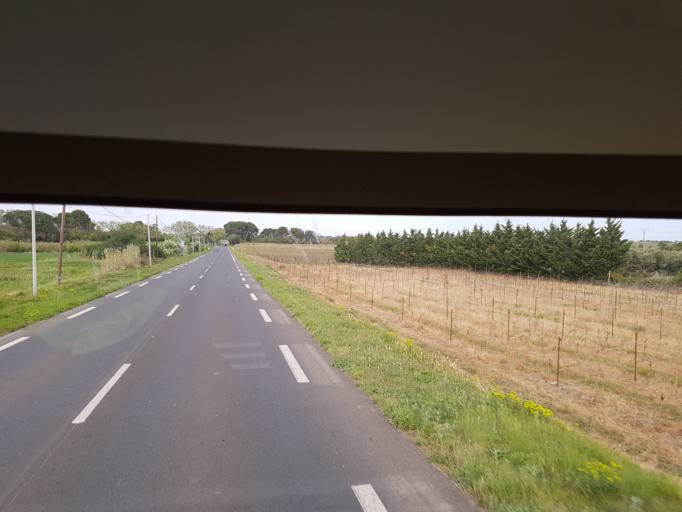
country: FR
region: Languedoc-Roussillon
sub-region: Departement de l'Herault
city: Agde
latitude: 43.3370
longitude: 3.4939
